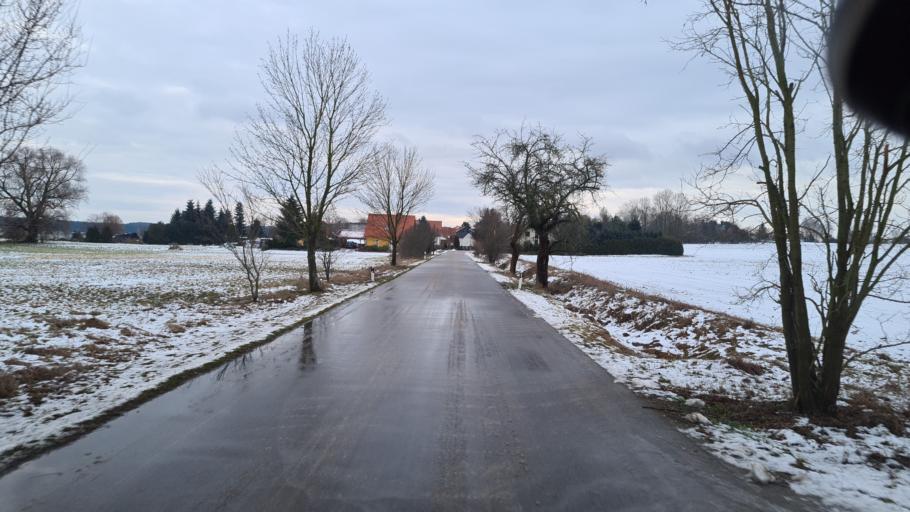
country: DE
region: Brandenburg
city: Schenkendobern
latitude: 51.9125
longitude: 14.5738
